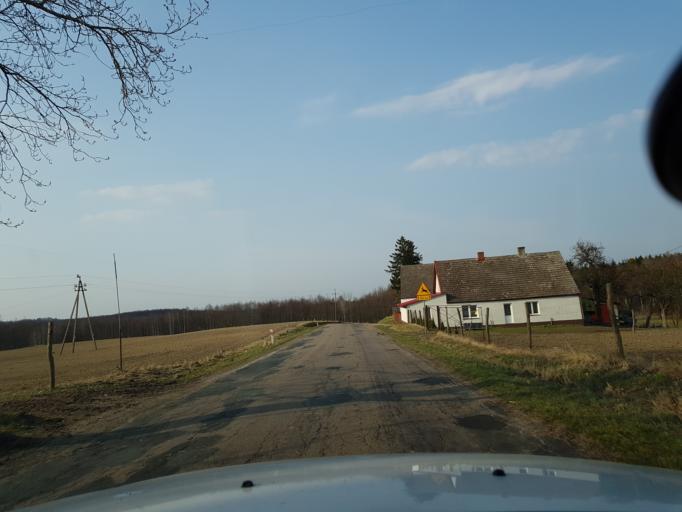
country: PL
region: West Pomeranian Voivodeship
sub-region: Powiat swidwinski
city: Polczyn-Zdroj
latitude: 53.7243
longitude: 16.0715
